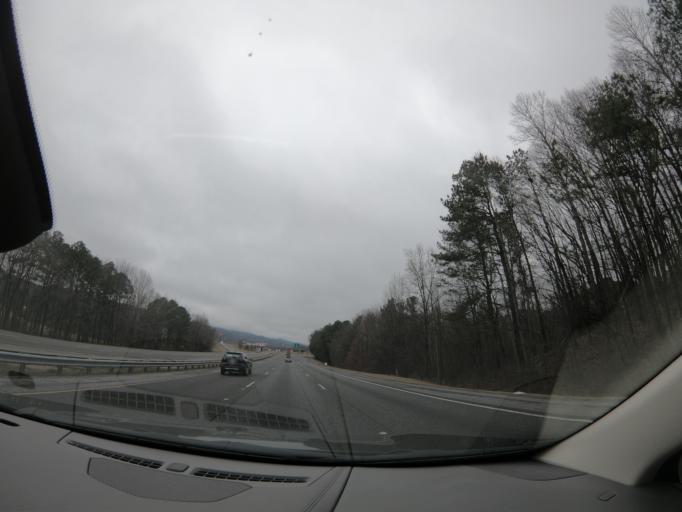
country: US
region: Georgia
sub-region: Whitfield County
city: Dalton
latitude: 34.6833
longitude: -85.0006
